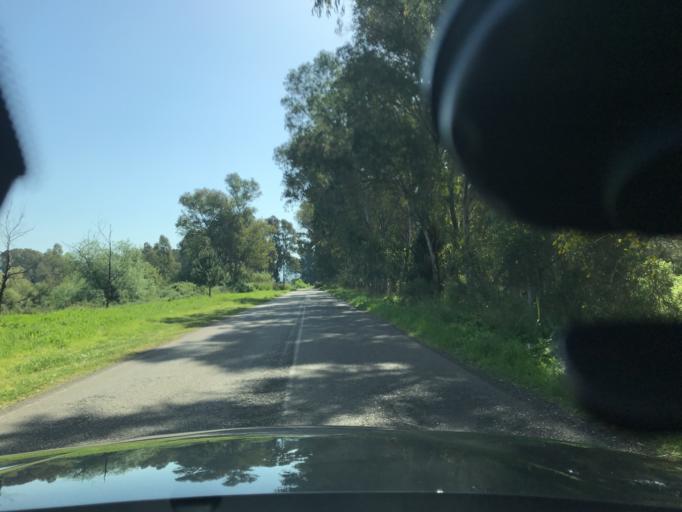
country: GR
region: West Greece
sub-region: Nomos Ileias
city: Epitalion
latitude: 37.6400
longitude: 21.4810
